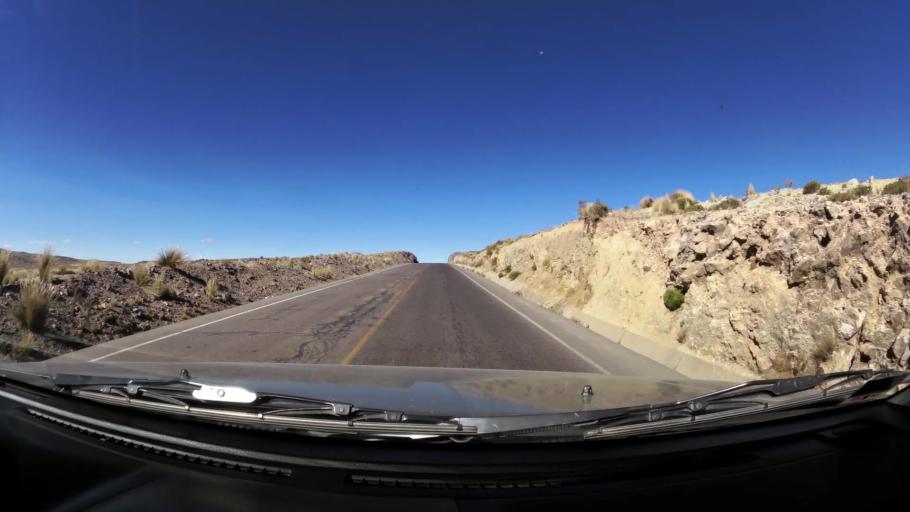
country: PE
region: Huancavelica
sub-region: Huaytara
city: Huayacundo Arma
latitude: -13.5386
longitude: -75.1858
